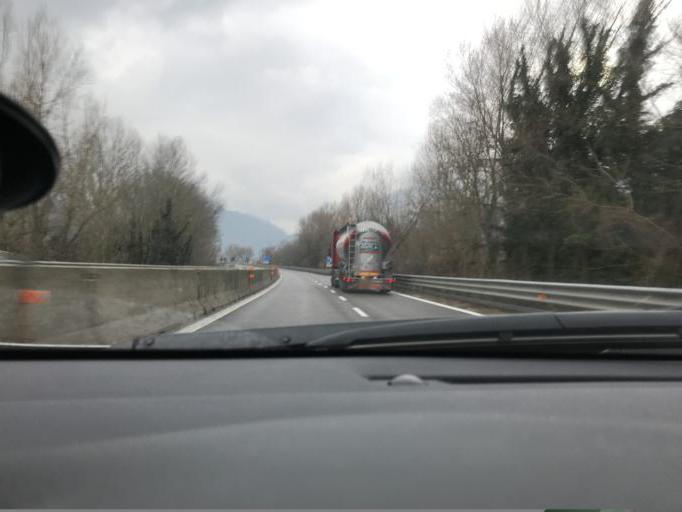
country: IT
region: The Marches
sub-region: Provincia di Ancona
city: Serra San Quirico
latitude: 43.4490
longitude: 13.0368
